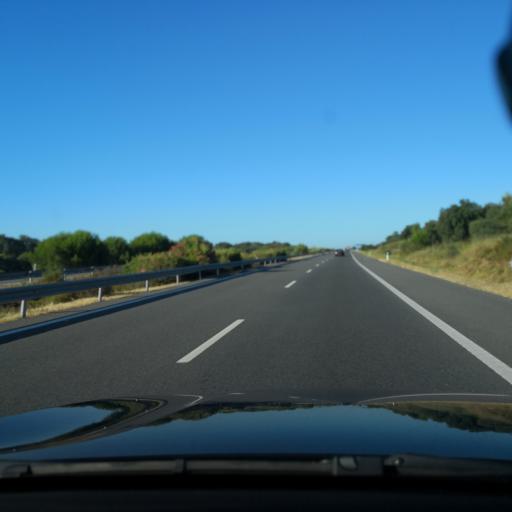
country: PT
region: Setubal
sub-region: Alcacer do Sal
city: Alcacer do Sal
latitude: 38.3462
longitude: -8.4982
